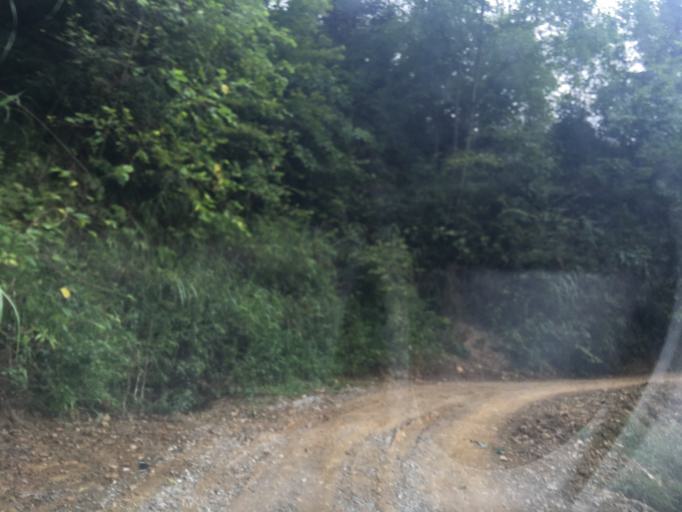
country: CN
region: Guangxi Zhuangzu Zizhiqu
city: Xinzhou
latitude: 25.1625
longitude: 105.6858
